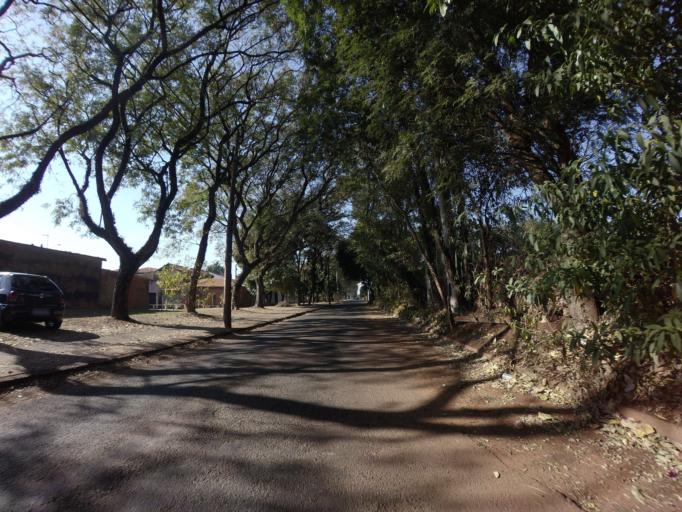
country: BR
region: Sao Paulo
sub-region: Piracicaba
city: Piracicaba
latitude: -22.7667
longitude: -47.5927
